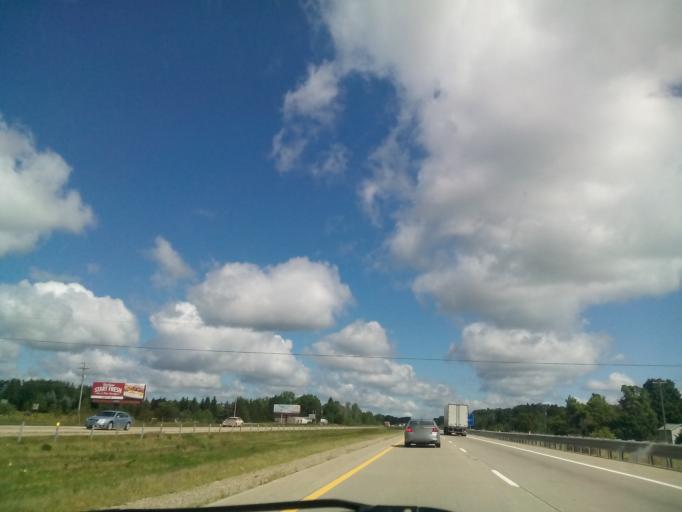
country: US
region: Michigan
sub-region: Genesee County
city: Linden
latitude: 42.7218
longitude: -83.7628
